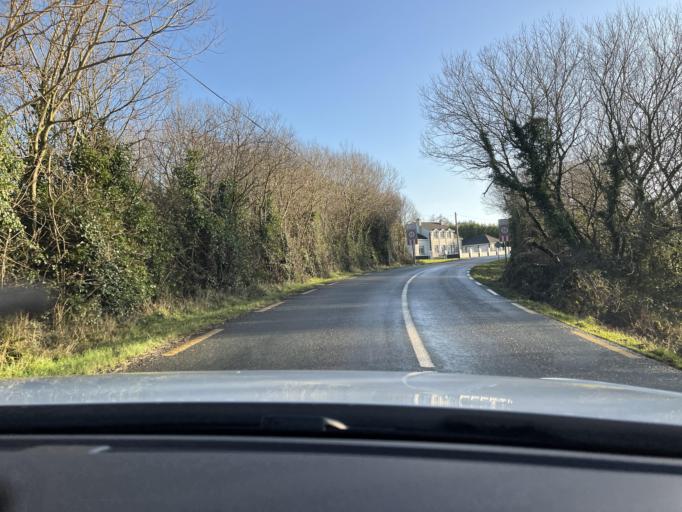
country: IE
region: Connaught
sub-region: County Leitrim
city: Manorhamilton
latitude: 54.2350
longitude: -8.2084
